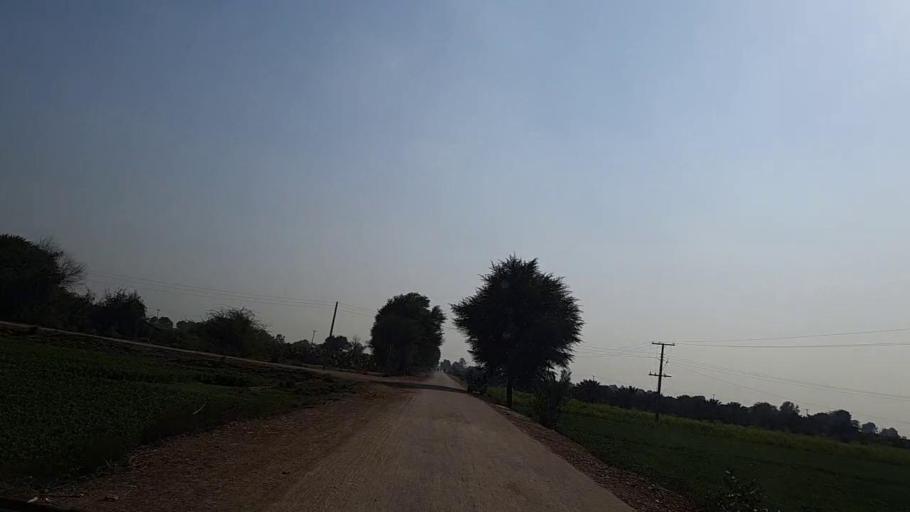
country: PK
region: Sindh
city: Sakrand
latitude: 26.0695
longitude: 68.2897
